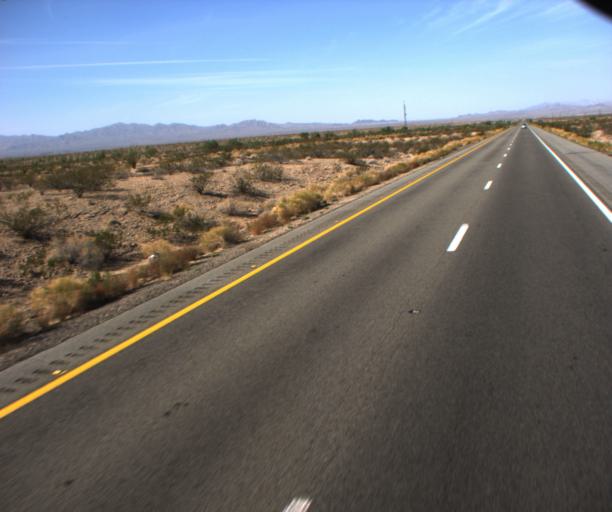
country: US
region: Arizona
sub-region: Mohave County
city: Desert Hills
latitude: 34.7832
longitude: -114.1774
